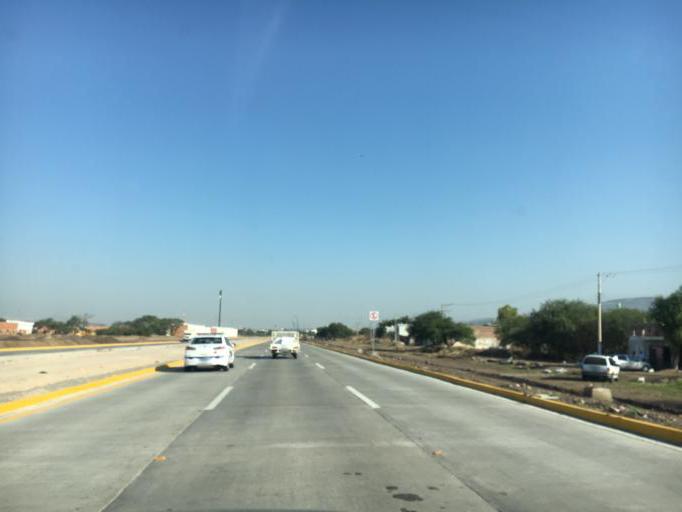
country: MX
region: Guanajuato
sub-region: Leon
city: Fraccionamiento Paraiso Real
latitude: 21.1108
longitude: -101.5855
